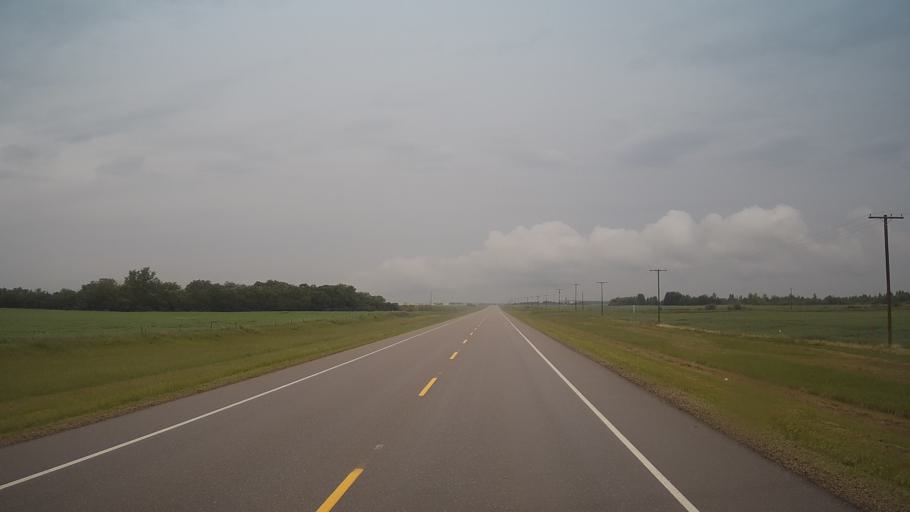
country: CA
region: Saskatchewan
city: Wilkie
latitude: 52.3159
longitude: -108.6974
